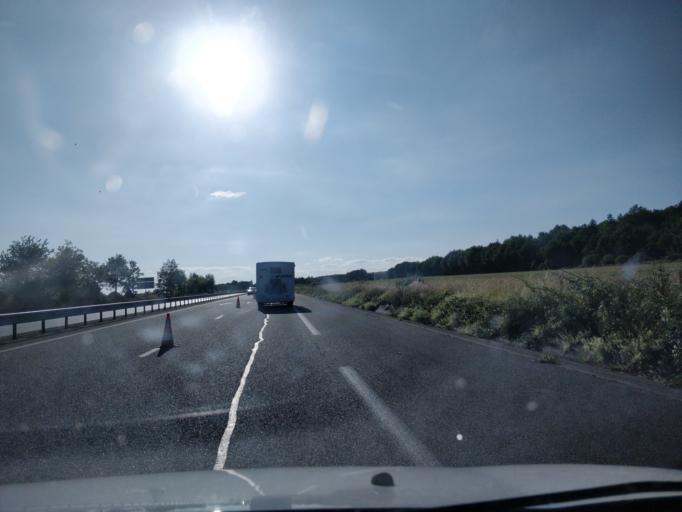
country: FR
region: Pays de la Loire
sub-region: Departement de Maine-et-Loire
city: Combree
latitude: 47.7171
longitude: -1.0209
